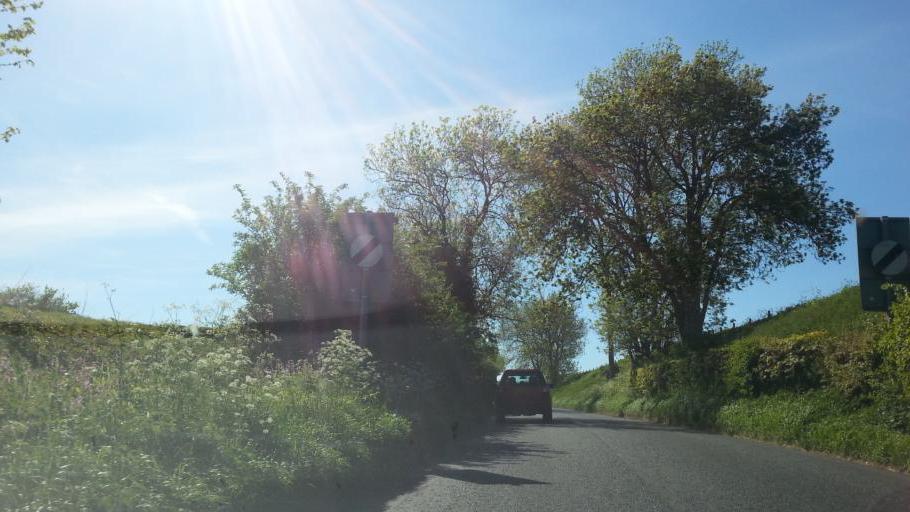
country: GB
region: England
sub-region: Dorset
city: Gillingham
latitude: 51.0011
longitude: -2.3134
